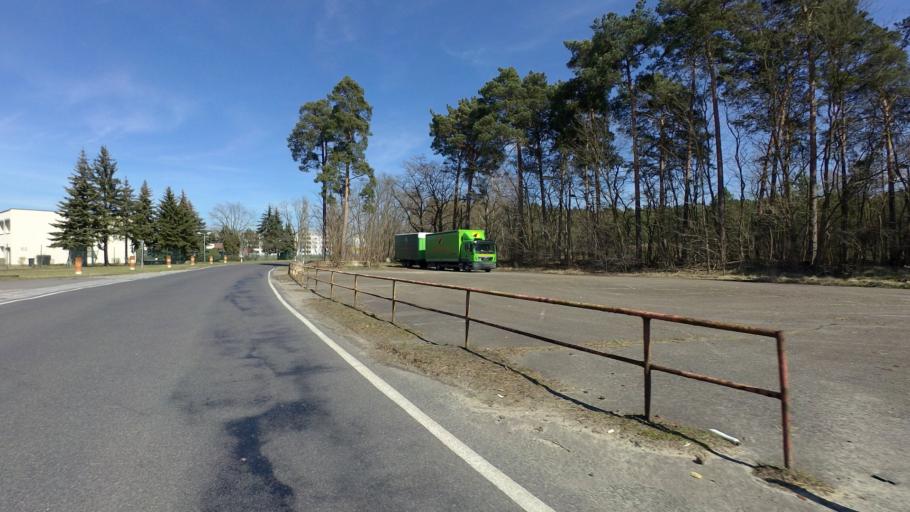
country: DE
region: Brandenburg
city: Storkow
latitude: 52.2356
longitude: 13.9474
